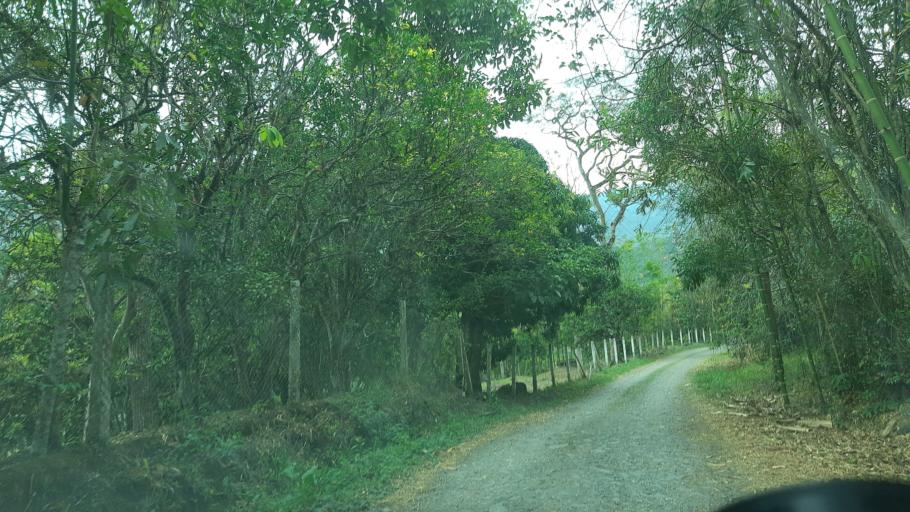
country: CO
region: Boyaca
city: Somondoco
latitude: 5.0084
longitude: -73.3681
